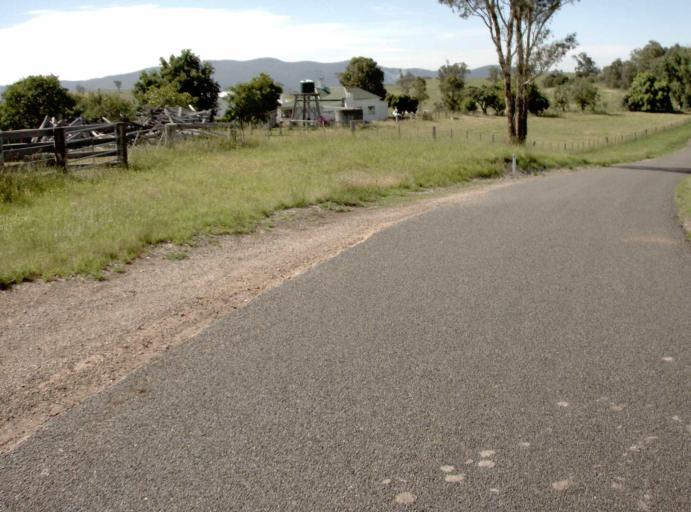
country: AU
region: Victoria
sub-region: East Gippsland
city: Lakes Entrance
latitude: -37.4888
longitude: 148.1303
